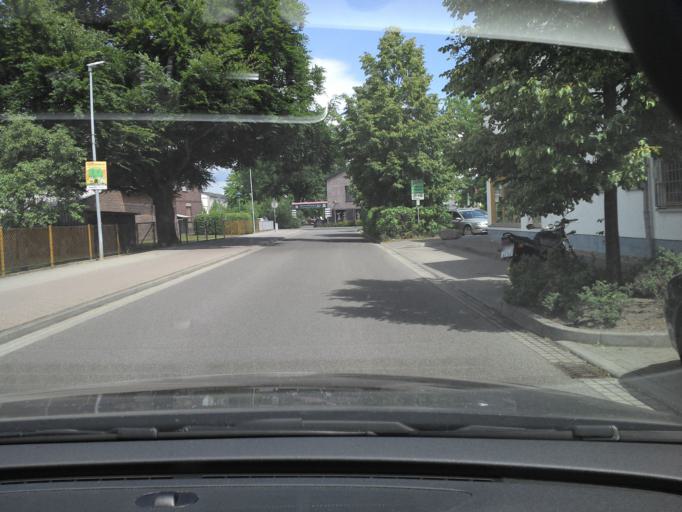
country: DE
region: Brandenburg
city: Burg
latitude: 51.8348
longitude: 14.1447
